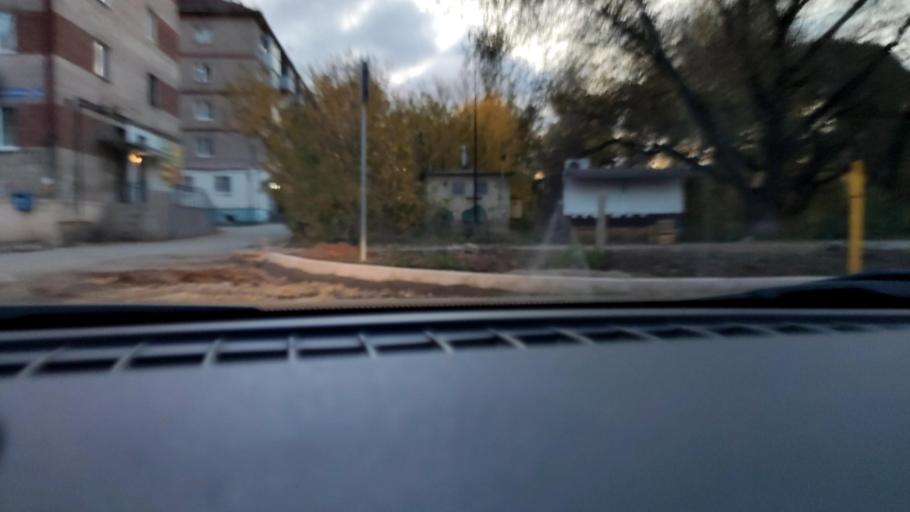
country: RU
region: Perm
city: Perm
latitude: 57.9717
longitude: 56.2747
